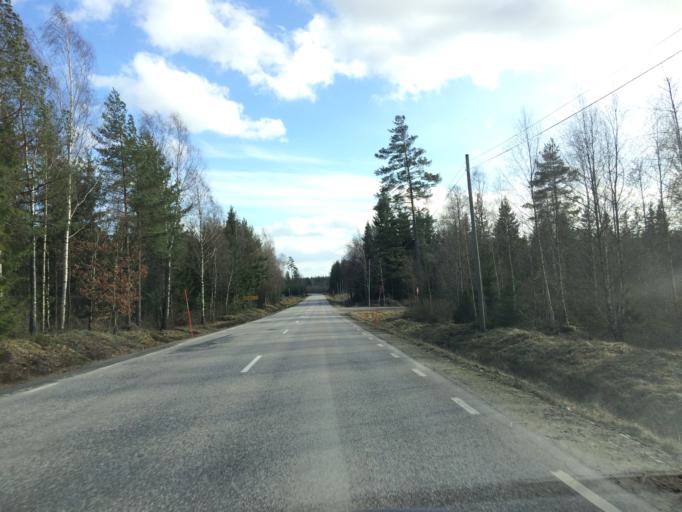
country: SE
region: Kronoberg
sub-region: Almhults Kommun
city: AElmhult
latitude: 56.5865
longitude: 14.0984
